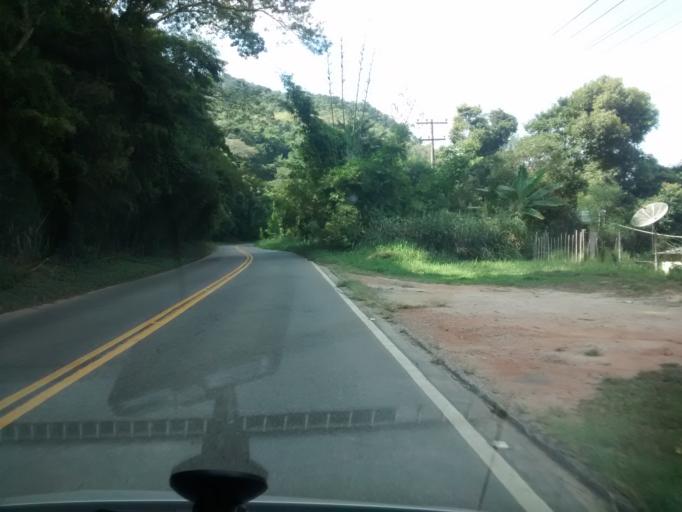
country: BR
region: Rio de Janeiro
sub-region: Miguel Pereira
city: Miguel Pereira
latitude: -22.4747
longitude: -43.5684
